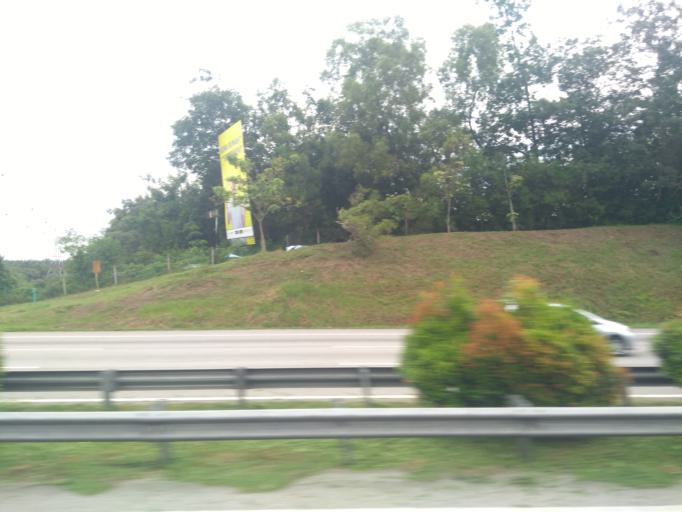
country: MY
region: Melaka
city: Pulau Sebang
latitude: 2.4234
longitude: 102.2130
